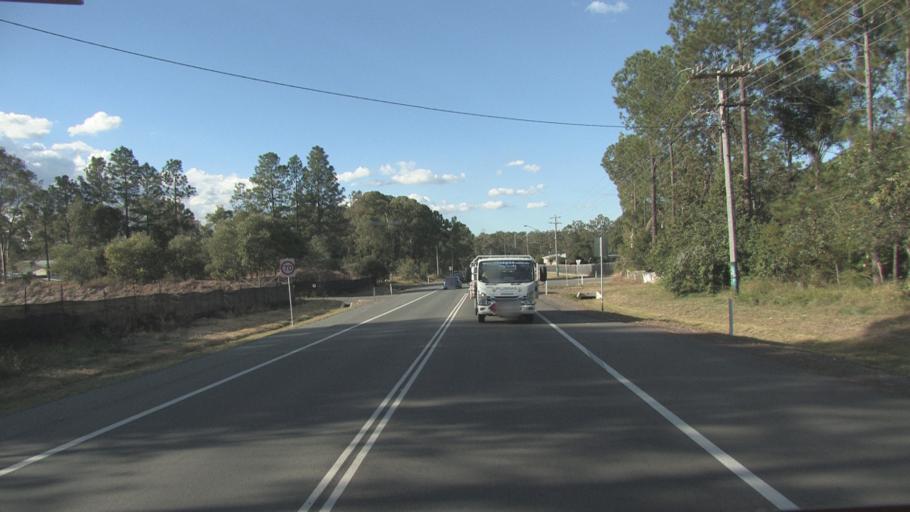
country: AU
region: Queensland
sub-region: Logan
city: Park Ridge South
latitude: -27.7186
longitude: 152.9697
